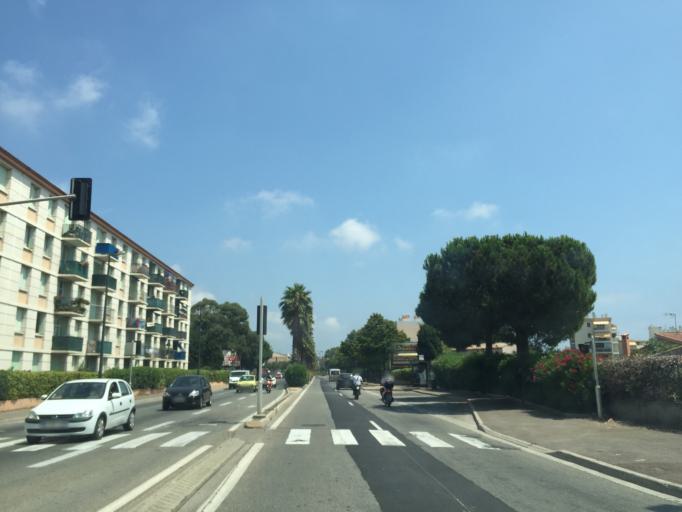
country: FR
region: Provence-Alpes-Cote d'Azur
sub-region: Departement du Var
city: Frejus
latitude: 43.4275
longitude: 6.7461
